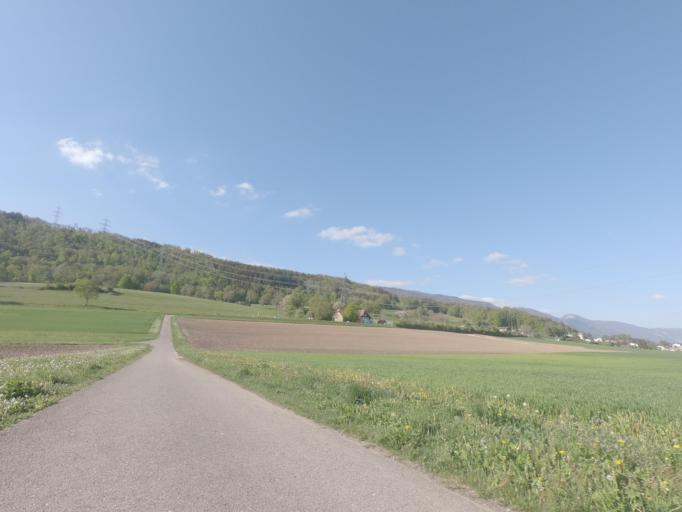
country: CH
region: Bern
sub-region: Biel/Bienne District
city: Pieterlen
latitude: 47.1749
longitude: 7.3499
